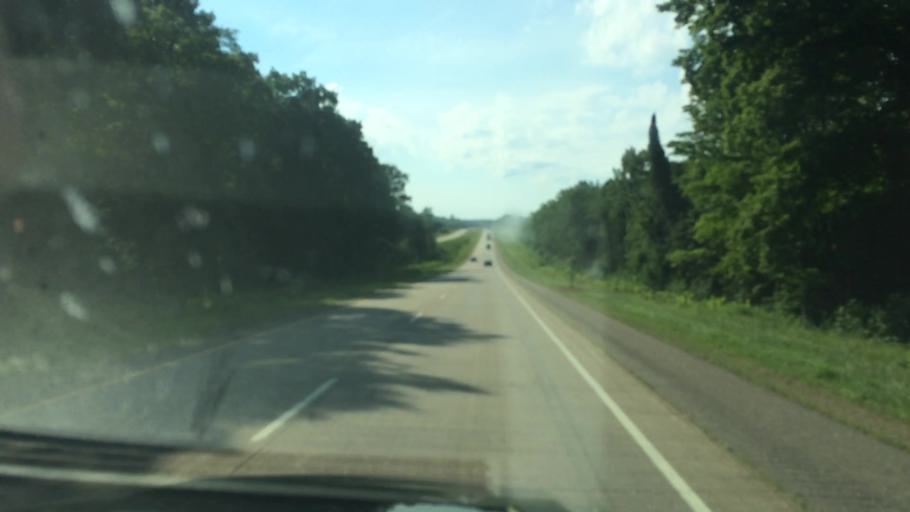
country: US
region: Wisconsin
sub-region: Shawano County
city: Wittenberg
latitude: 44.8172
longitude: -89.0509
